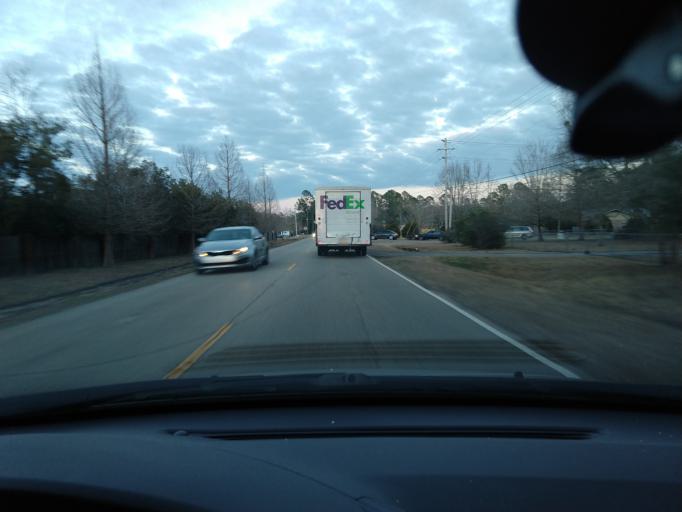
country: US
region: Mississippi
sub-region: Jackson County
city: Gulf Park Estates
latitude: 30.4201
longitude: -88.7646
